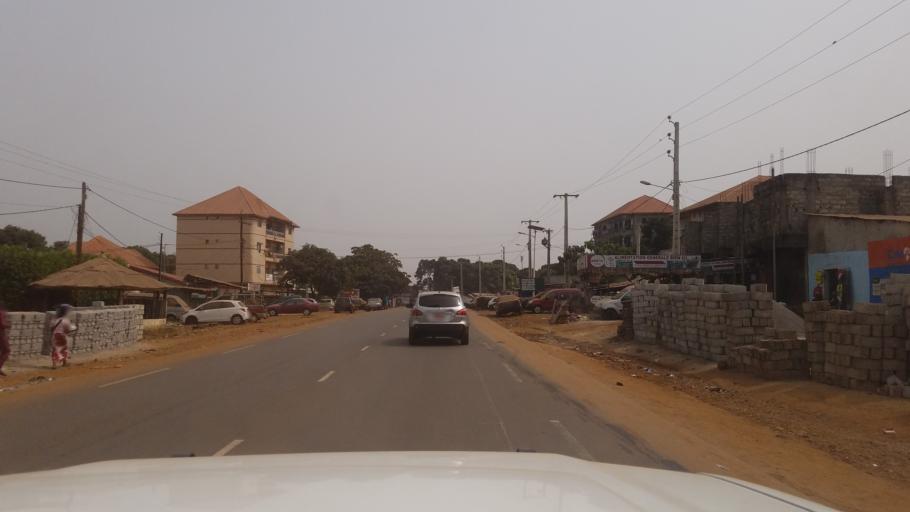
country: GN
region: Kindia
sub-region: Prefecture de Dubreka
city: Dubreka
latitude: 9.6692
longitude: -13.5856
